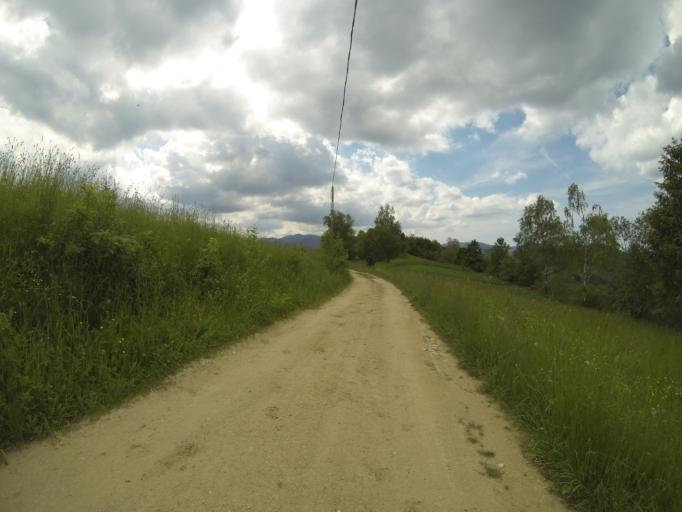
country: RO
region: Brasov
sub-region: Comuna Poiana Marului
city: Poiana Marului
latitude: 45.6235
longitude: 25.3142
